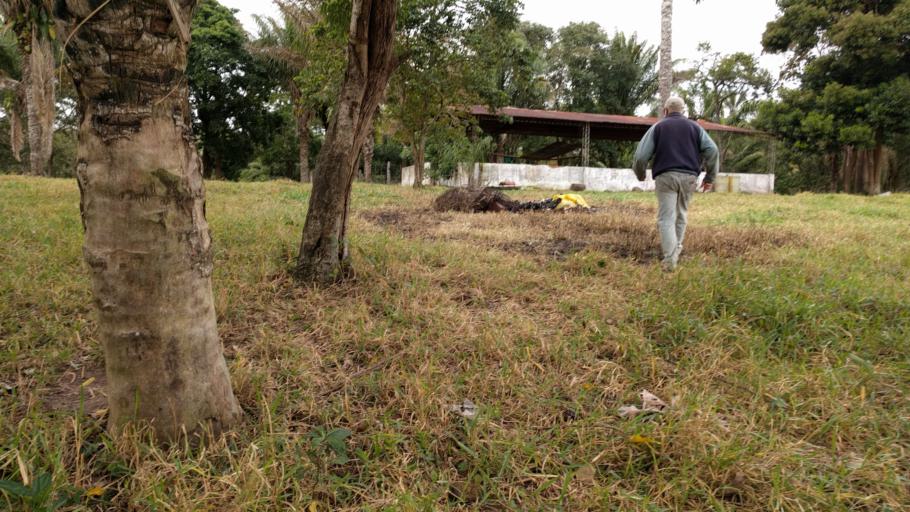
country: BO
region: Santa Cruz
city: San Juan del Surutu
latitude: -17.4590
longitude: -63.6976
